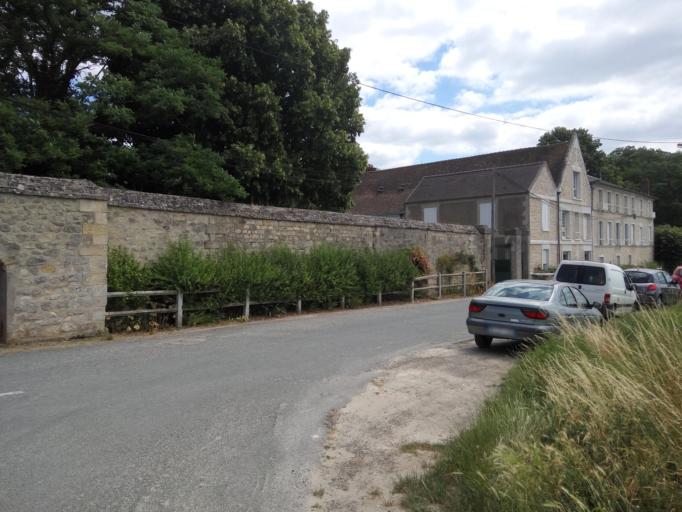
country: FR
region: Picardie
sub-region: Departement de l'Oise
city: Boran-sur-Oise
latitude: 49.1604
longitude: 2.3508
